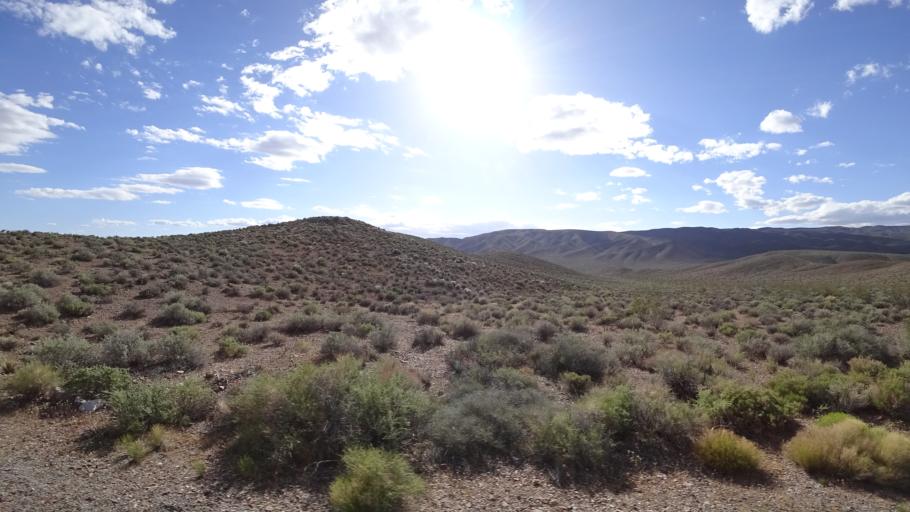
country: US
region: California
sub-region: San Bernardino County
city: Searles Valley
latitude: 36.2954
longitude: -117.1753
